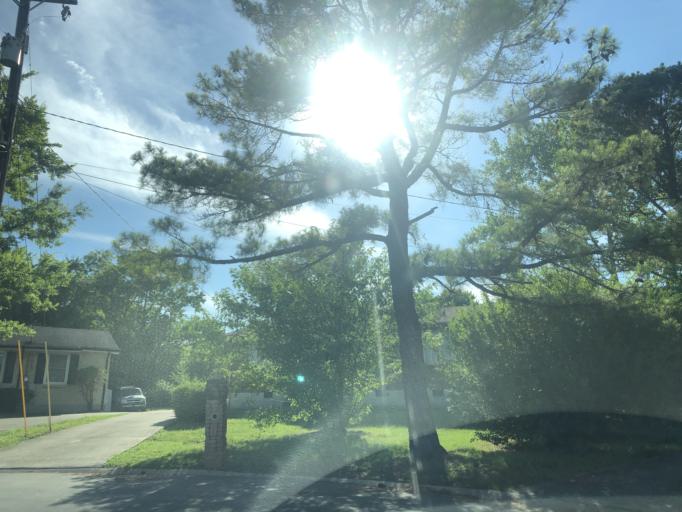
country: US
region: Tennessee
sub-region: Davidson County
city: Nashville
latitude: 36.2135
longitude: -86.8344
